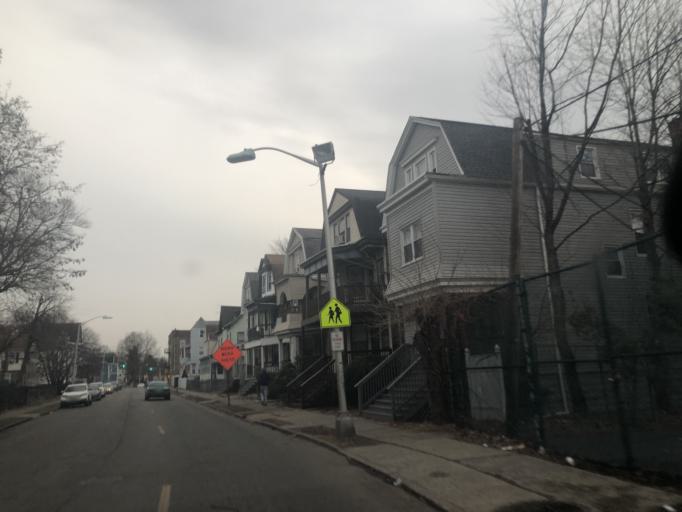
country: US
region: New Jersey
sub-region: Essex County
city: East Orange
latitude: 40.7702
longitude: -74.2085
